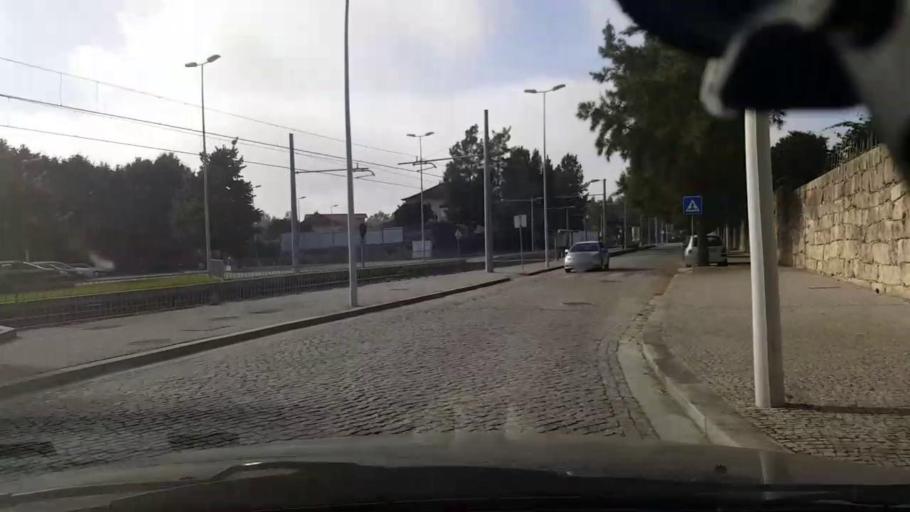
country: PT
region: Porto
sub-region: Maia
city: Gemunde
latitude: 41.2696
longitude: -8.6787
